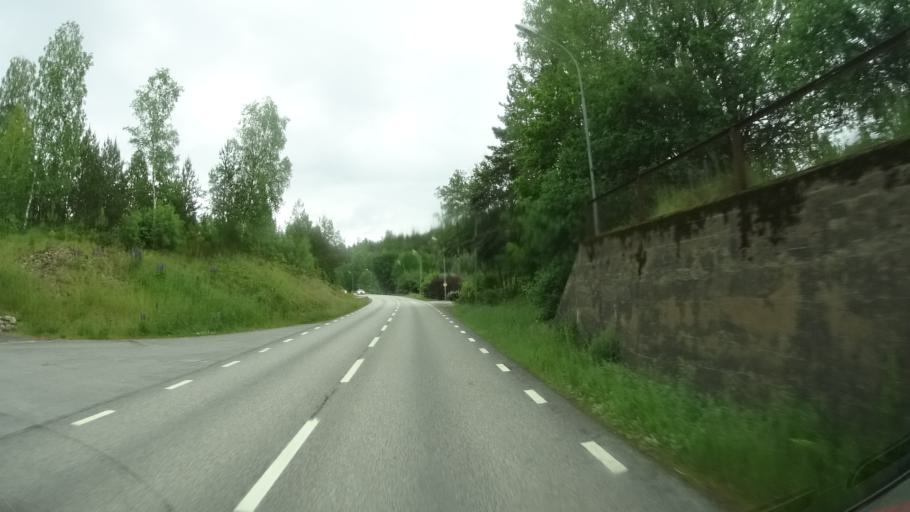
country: SE
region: Kalmar
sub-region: Hultsfreds Kommun
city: Hultsfred
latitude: 57.5370
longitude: 15.7606
